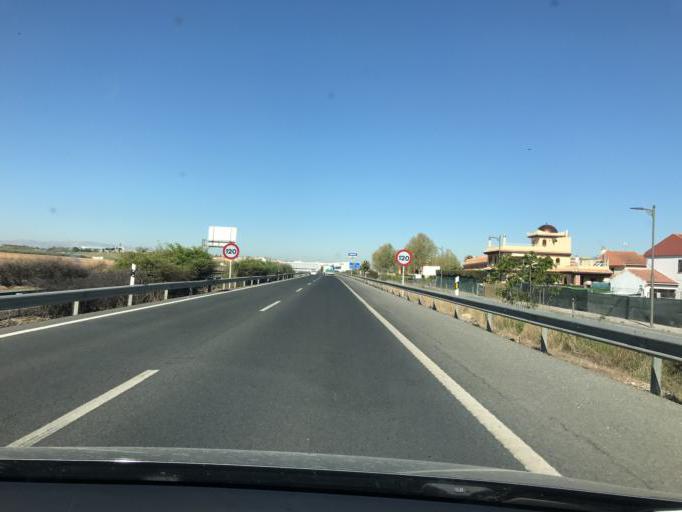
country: ES
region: Andalusia
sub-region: Provincia de Granada
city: Cijuela
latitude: 37.1952
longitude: -3.8116
